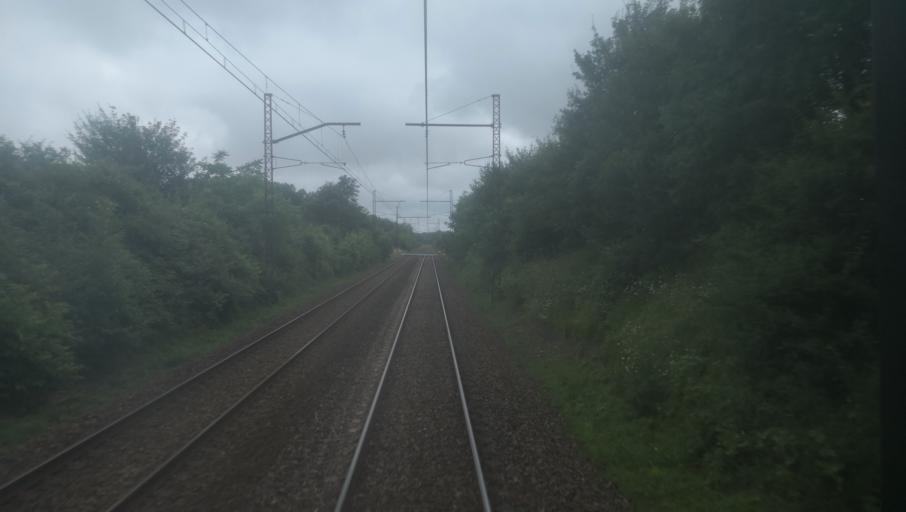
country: FR
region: Centre
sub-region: Departement du Cher
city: Mereau
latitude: 47.1482
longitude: 2.0511
